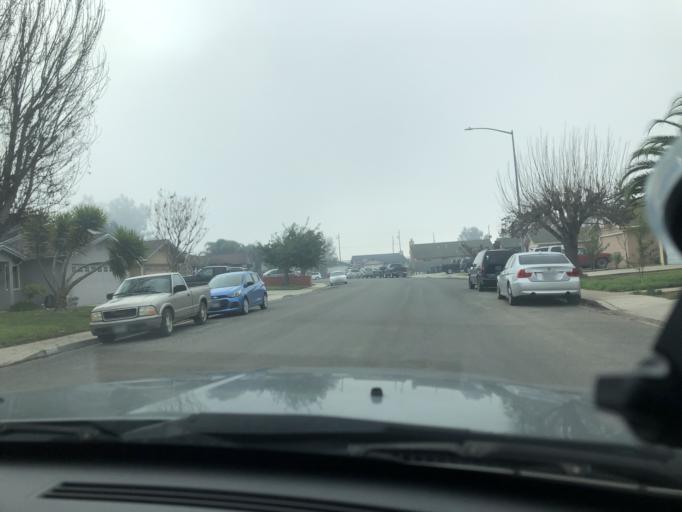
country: US
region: California
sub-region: Monterey County
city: King City
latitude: 36.2054
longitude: -121.1416
